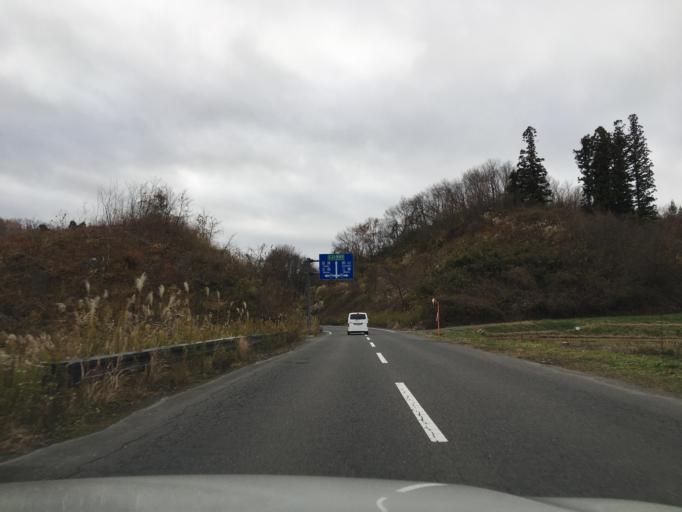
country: JP
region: Fukushima
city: Miharu
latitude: 37.4481
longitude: 140.5277
